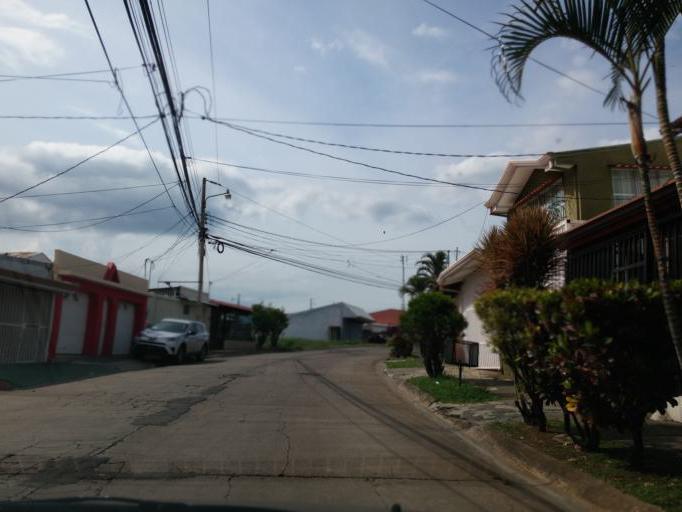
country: CR
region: Alajuela
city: Alajuela
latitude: 10.0101
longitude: -84.1953
